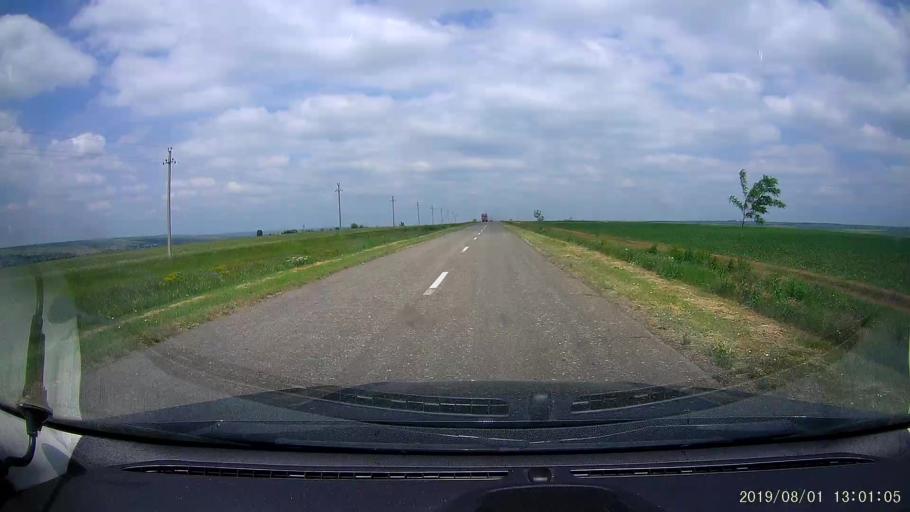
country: MD
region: Gagauzia
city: Vulcanesti
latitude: 45.7318
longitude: 28.3989
